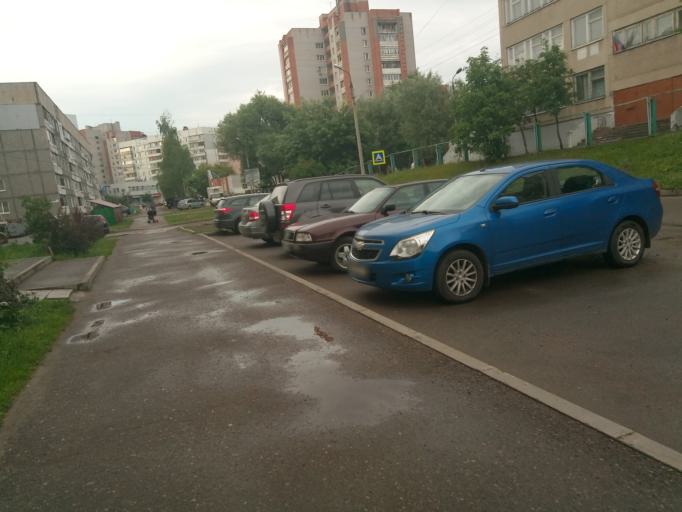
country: RU
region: Jaroslavl
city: Yaroslavl
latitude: 57.6494
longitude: 39.9586
